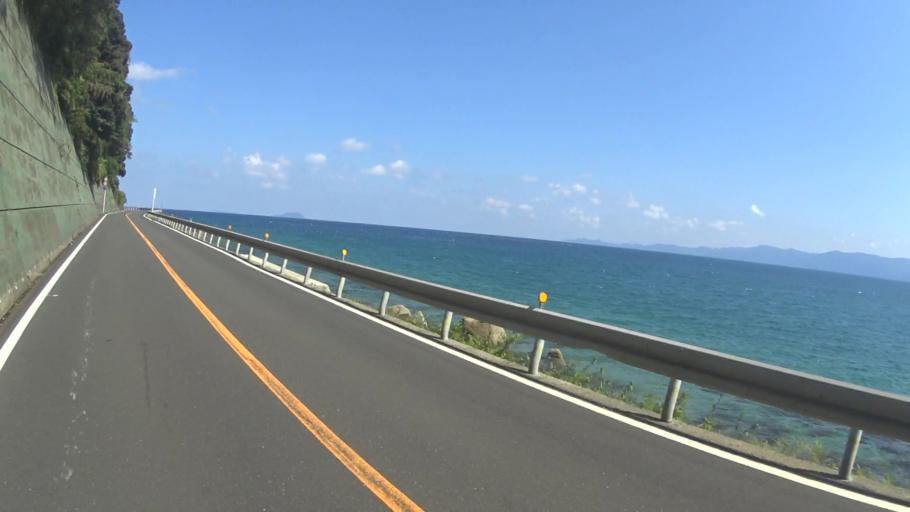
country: JP
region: Kyoto
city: Miyazu
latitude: 35.6194
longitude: 135.2430
